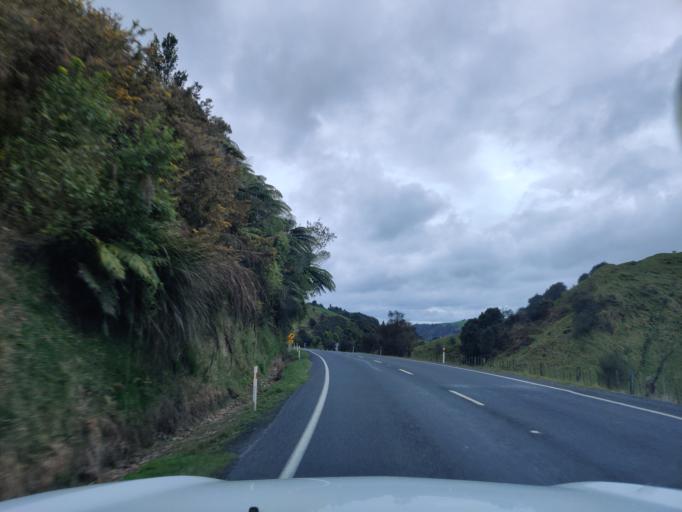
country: NZ
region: Waikato
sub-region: Otorohanga District
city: Otorohanga
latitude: -38.5105
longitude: 175.2068
